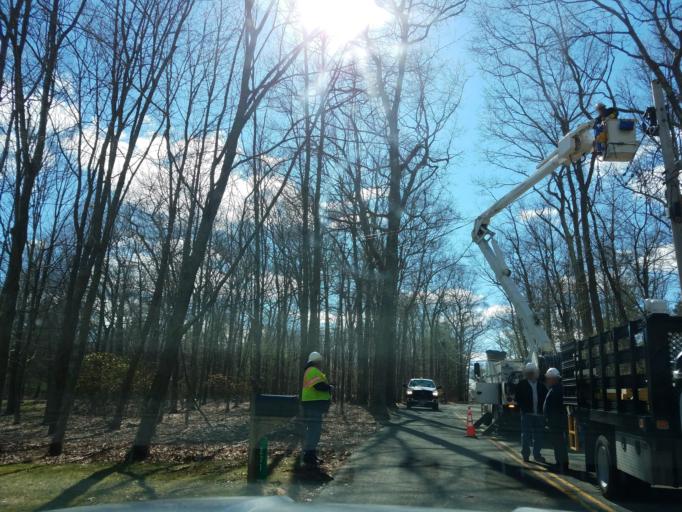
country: US
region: Connecticut
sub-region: Windham County
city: North Grosvenor Dale
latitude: 41.9985
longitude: -71.8818
